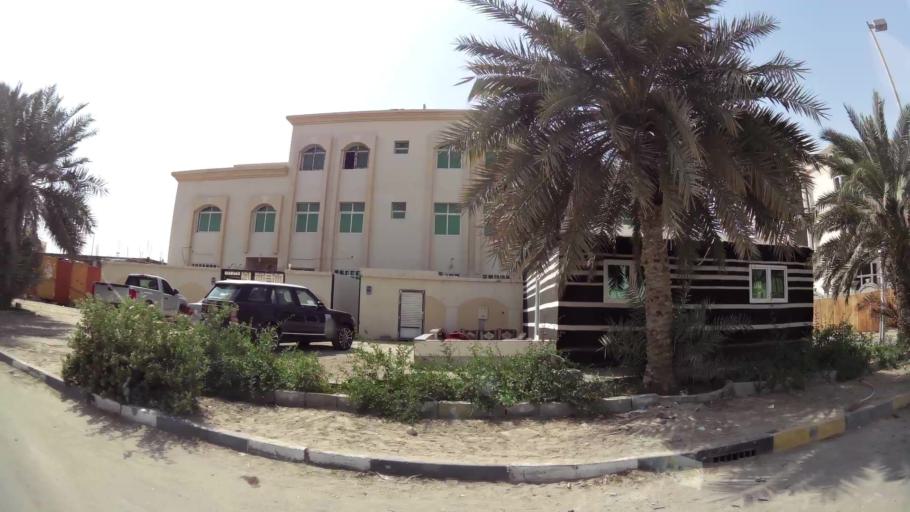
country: AE
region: Abu Dhabi
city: Abu Dhabi
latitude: 24.3006
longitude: 54.6405
